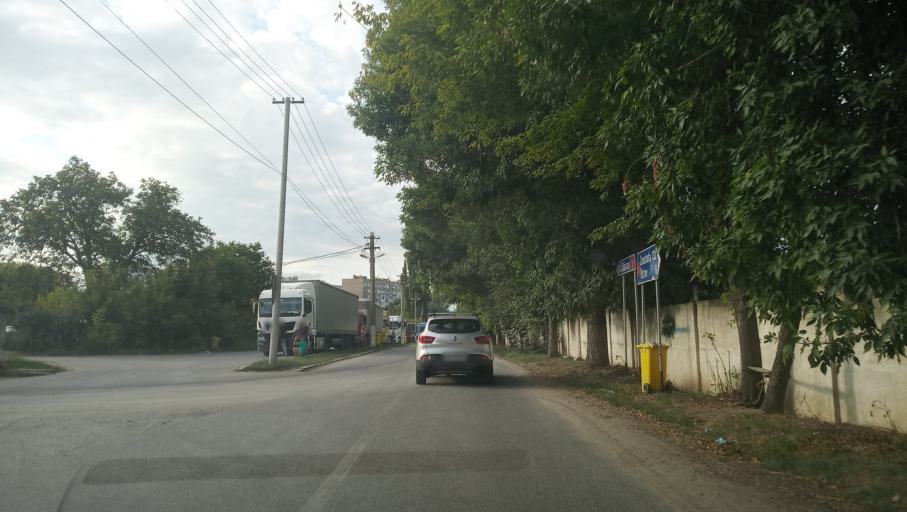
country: BG
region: Silistra
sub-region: Obshtina Silistra
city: Silistra
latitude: 44.1176
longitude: 27.2774
